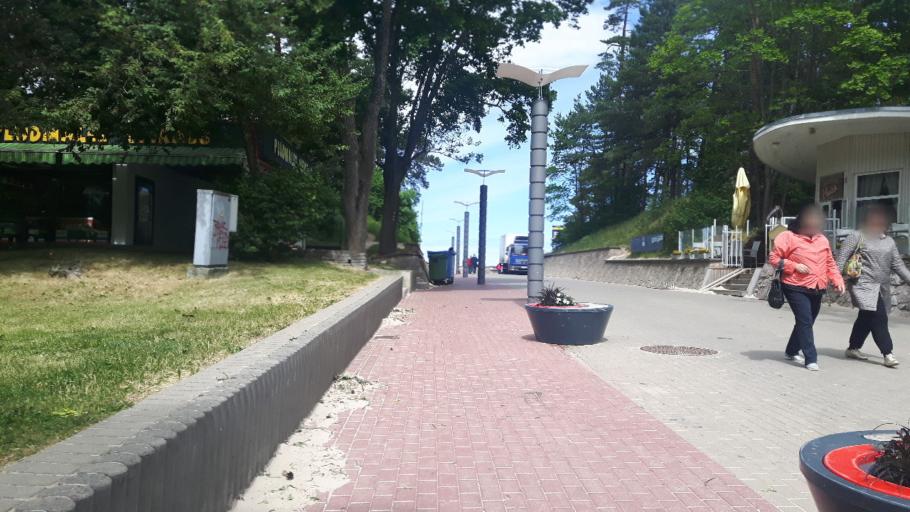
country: LV
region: Jurmala
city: Jurmala
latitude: 56.9778
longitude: 23.8114
